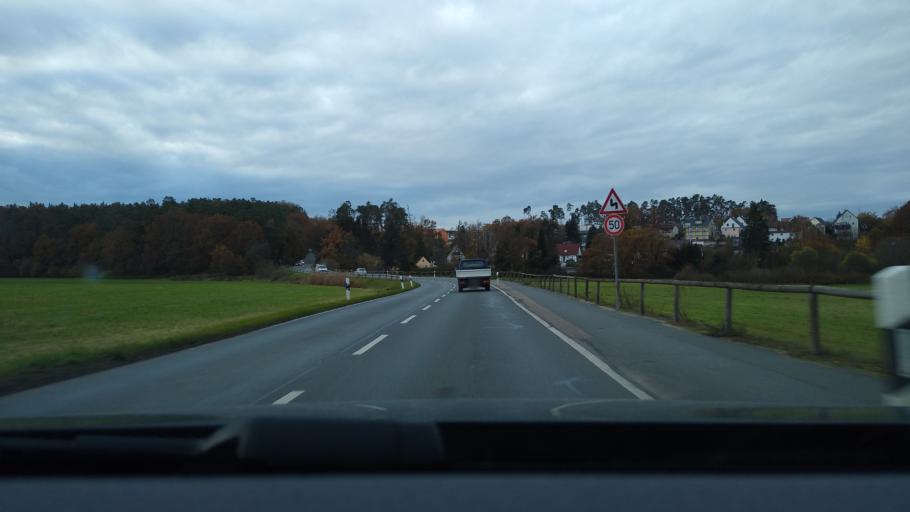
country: DE
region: Bavaria
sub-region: Regierungsbezirk Mittelfranken
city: Schwabach
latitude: 49.3478
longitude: 11.0521
